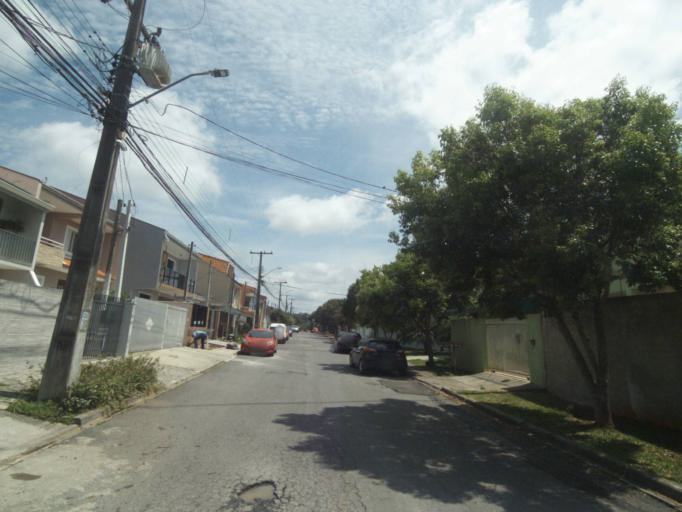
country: BR
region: Parana
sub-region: Curitiba
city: Curitiba
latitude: -25.4573
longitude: -49.3575
